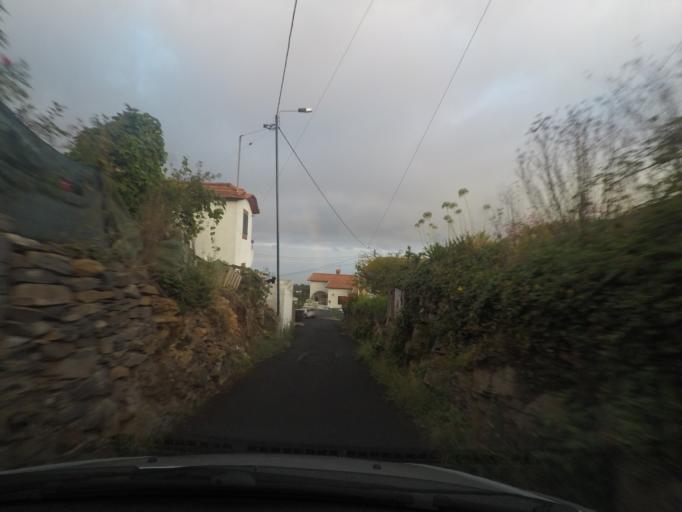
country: PT
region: Madeira
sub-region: Santa Cruz
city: Camacha
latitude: 32.6814
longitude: -16.8527
